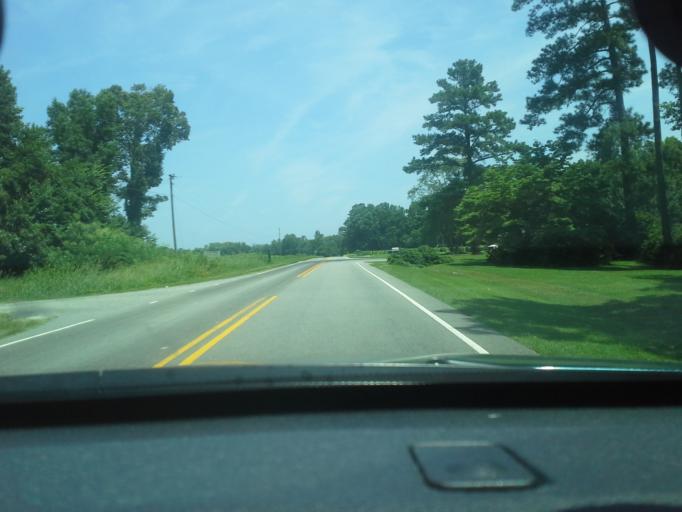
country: US
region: North Carolina
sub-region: Chowan County
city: Edenton
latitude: 35.9301
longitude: -76.5749
